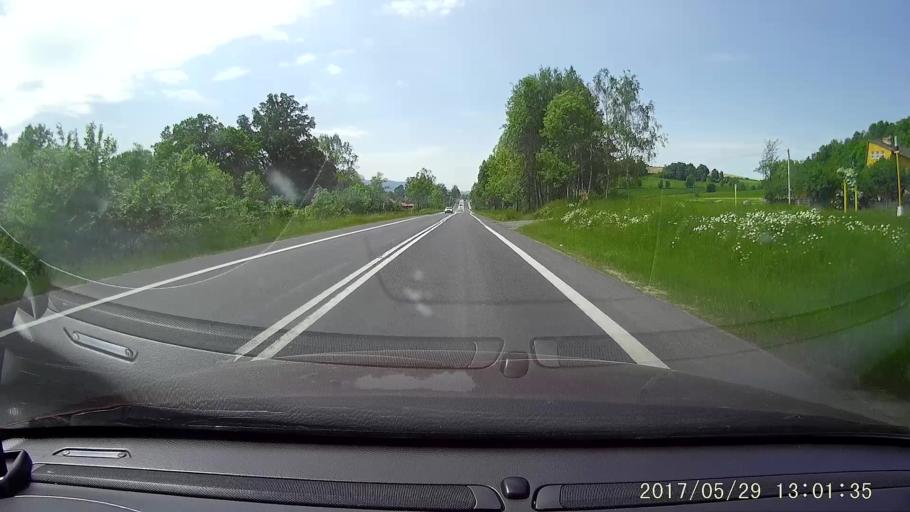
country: PL
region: Lower Silesian Voivodeship
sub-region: Jelenia Gora
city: Cieplice Slaskie Zdroj
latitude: 50.9121
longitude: 15.6443
